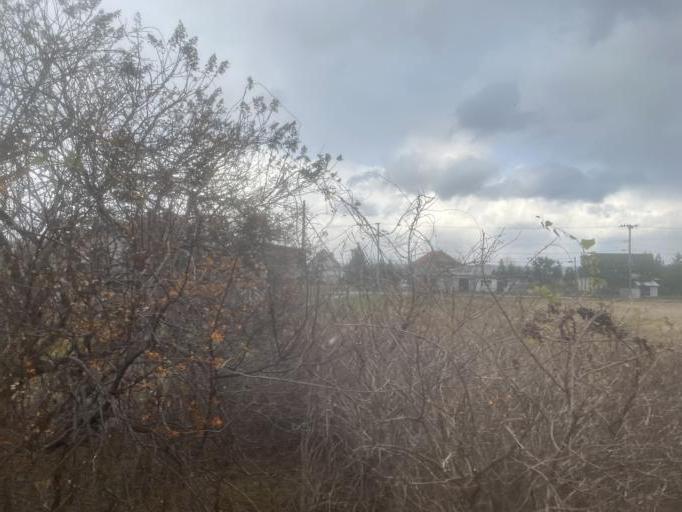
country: JP
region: Aomori
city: Shimokizukuri
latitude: 41.1807
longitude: 140.4710
